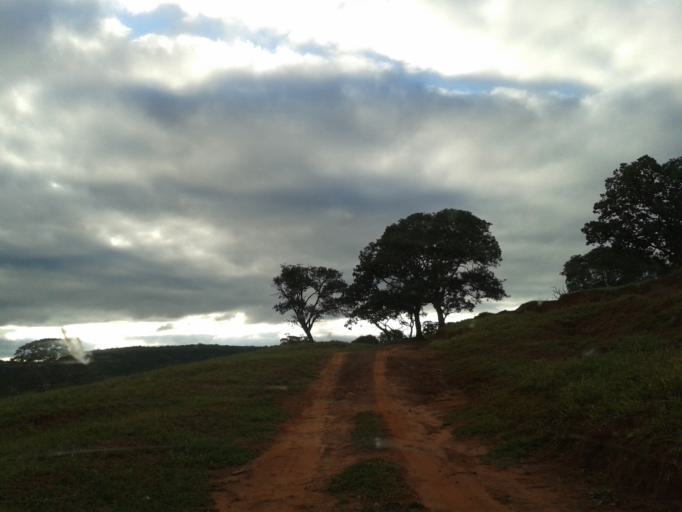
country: BR
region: Minas Gerais
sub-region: Campina Verde
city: Campina Verde
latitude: -19.4692
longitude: -49.6506
